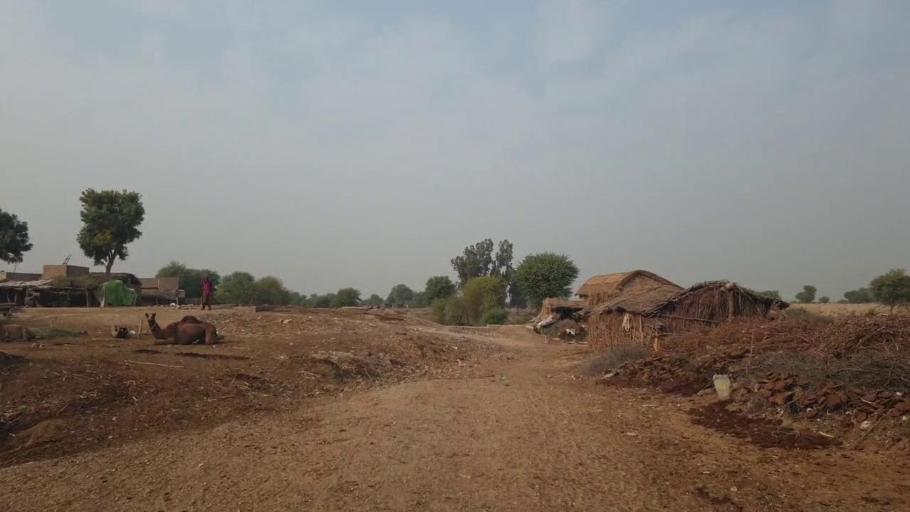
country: PK
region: Sindh
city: Sann
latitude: 26.0909
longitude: 68.0947
